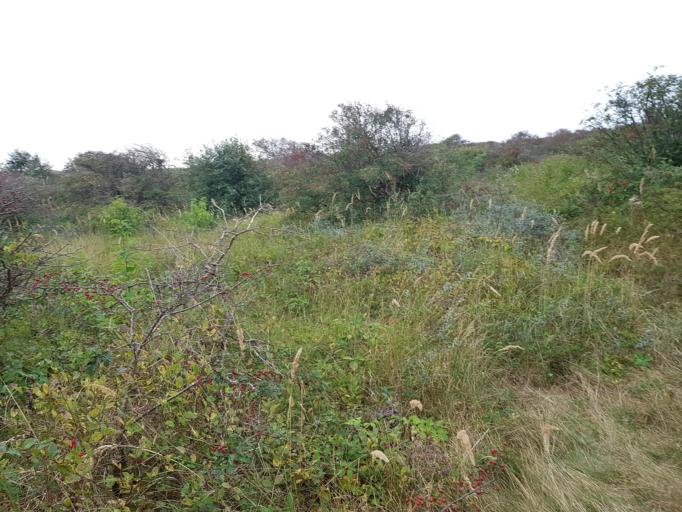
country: NL
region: North Holland
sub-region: Gemeente Texel
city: Den Burg
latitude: 53.0747
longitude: 4.7427
